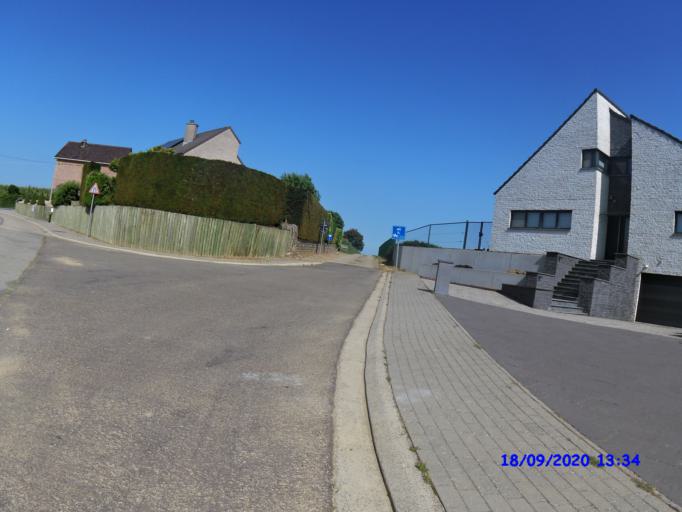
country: BE
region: Flanders
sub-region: Provincie Limburg
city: Gingelom
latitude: 50.7252
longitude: 5.1315
